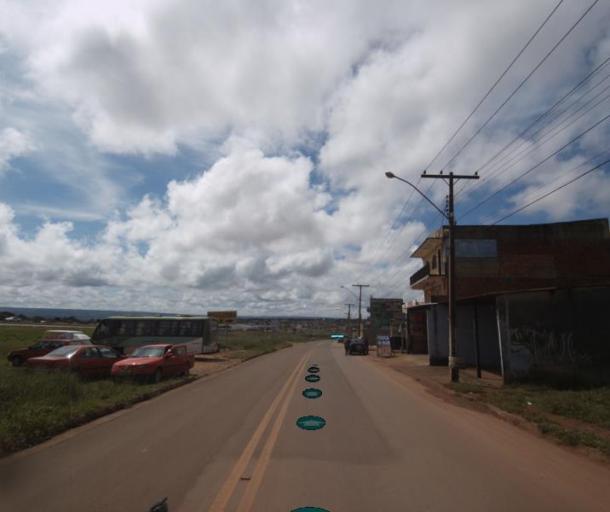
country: BR
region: Federal District
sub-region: Brasilia
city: Brasilia
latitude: -15.7361
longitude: -48.2790
